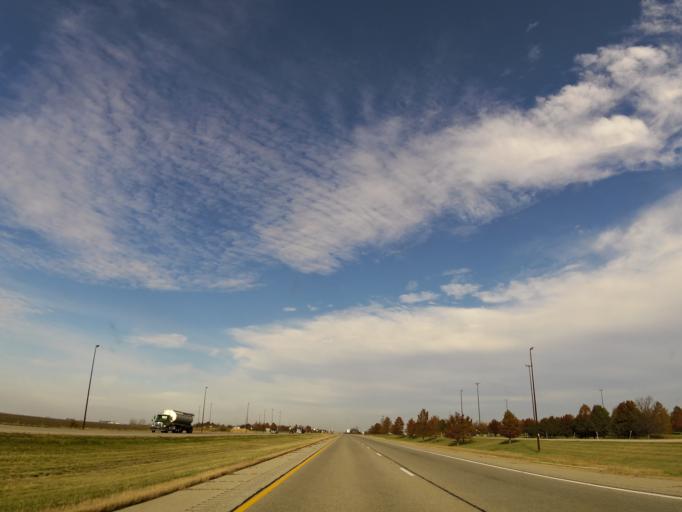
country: US
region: Illinois
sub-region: De Witt County
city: Farmer City
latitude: 40.2688
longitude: -88.6683
